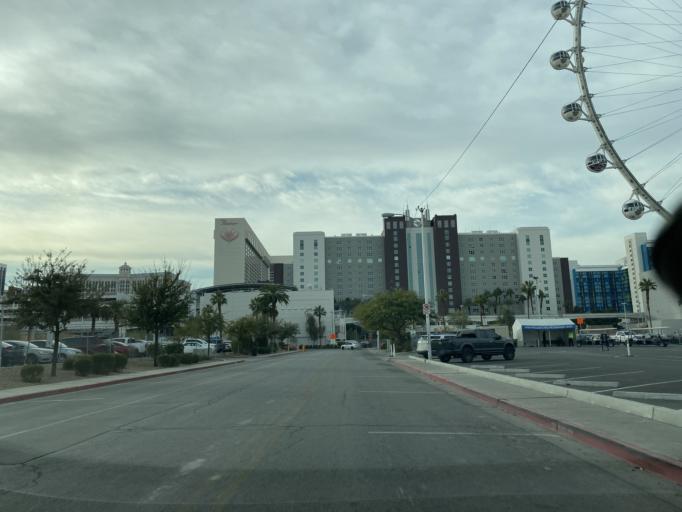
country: US
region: Nevada
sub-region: Clark County
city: Paradise
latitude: 36.1163
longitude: -115.1665
